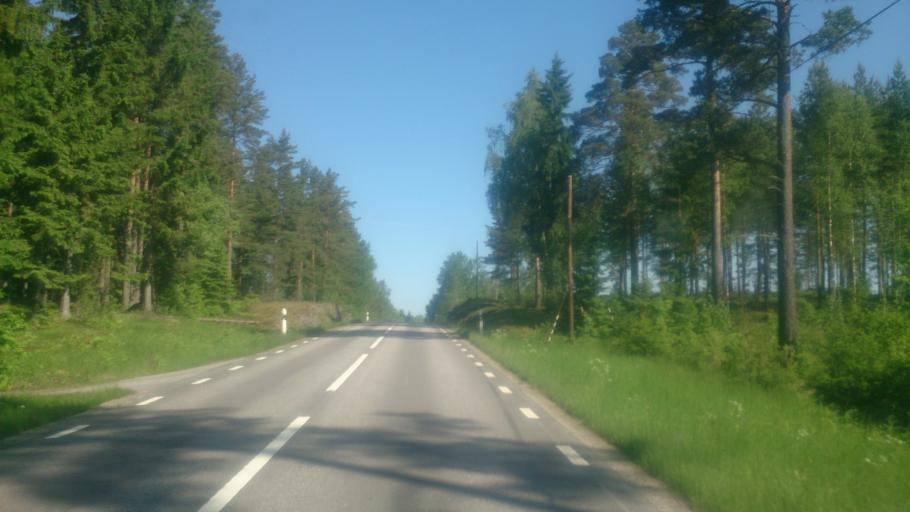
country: SE
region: OEstergoetland
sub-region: Atvidabergs Kommun
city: Atvidaberg
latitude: 58.1333
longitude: 16.0923
